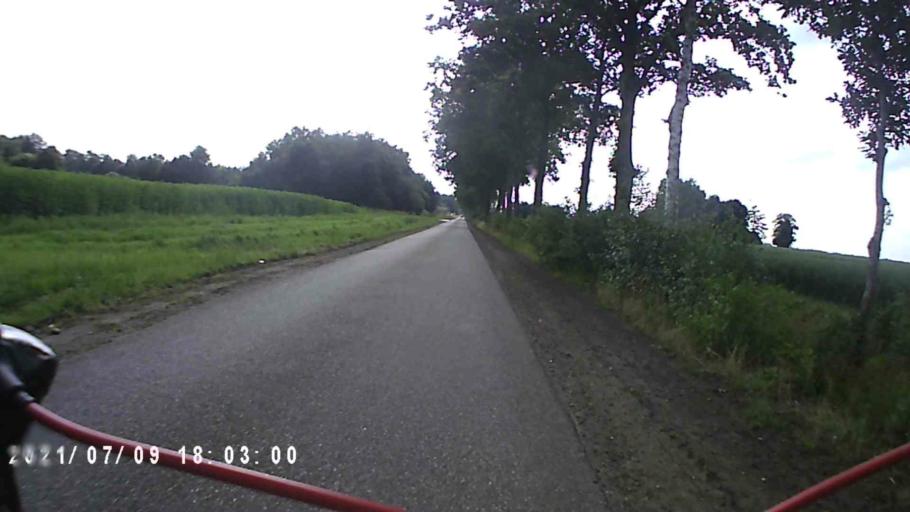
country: NL
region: Groningen
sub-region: Gemeente Pekela
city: Oude Pekela
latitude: 53.0687
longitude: 7.0473
